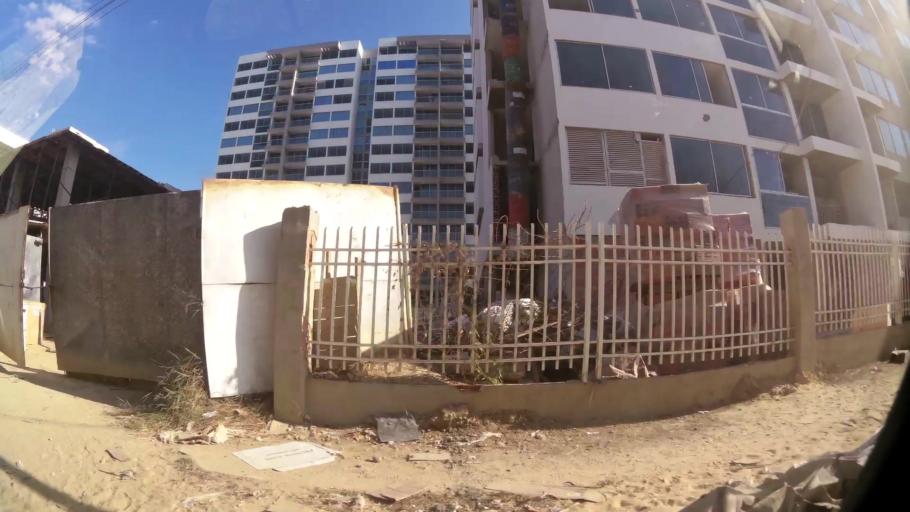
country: CO
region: Atlantico
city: Barranquilla
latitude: 11.0071
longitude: -74.8379
